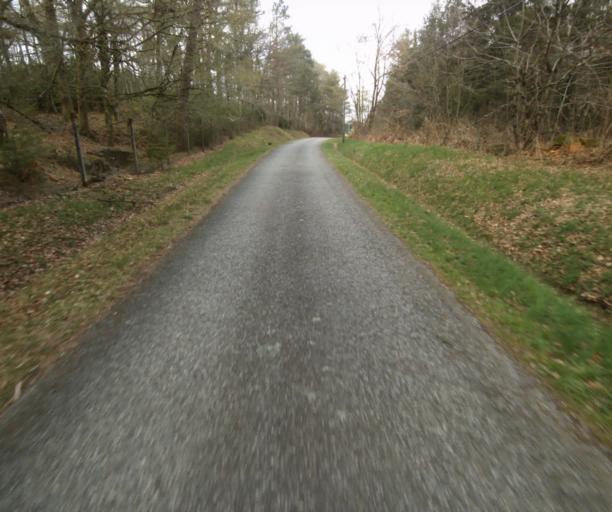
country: FR
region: Limousin
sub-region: Departement de la Correze
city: Correze
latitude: 45.2827
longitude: 1.9309
